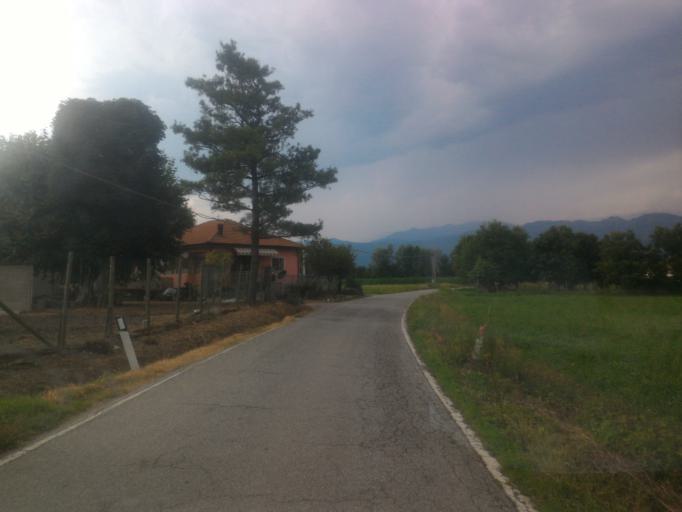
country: IT
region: Piedmont
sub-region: Provincia di Torino
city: Riva
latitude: 44.8889
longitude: 7.3976
